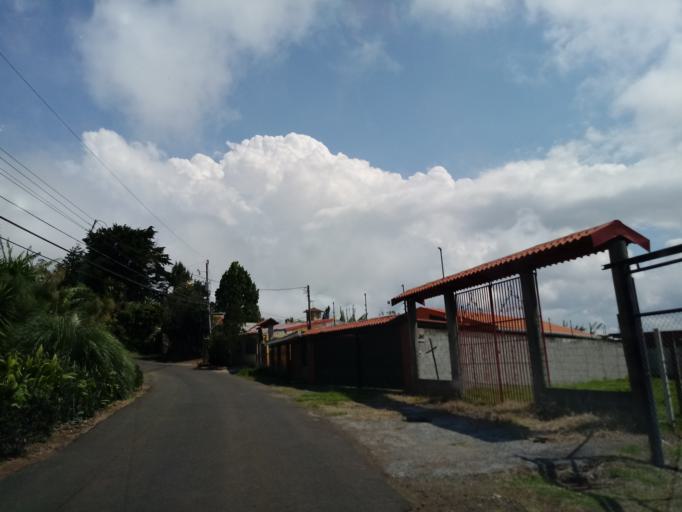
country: CR
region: Heredia
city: Angeles
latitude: 10.0298
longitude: -84.0359
